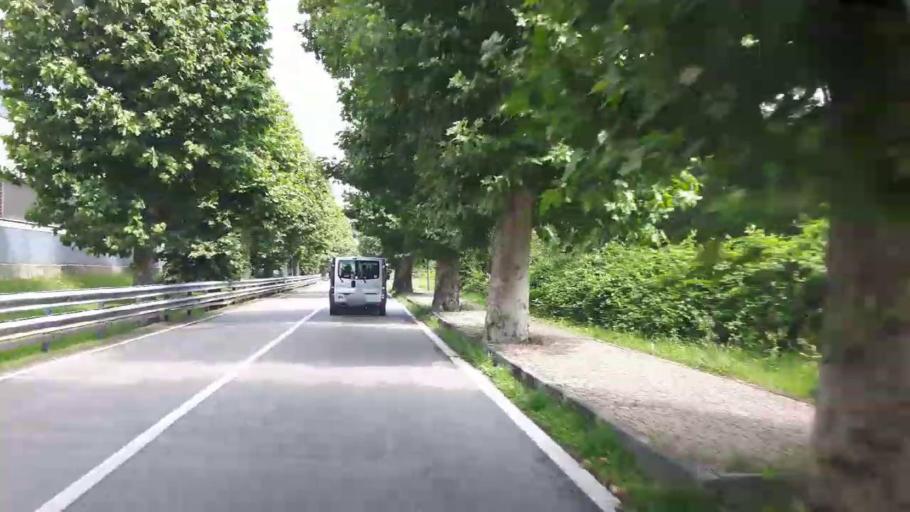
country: IT
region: Piedmont
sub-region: Provincia Verbano-Cusio-Ossola
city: Gravellona Toce
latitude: 45.9370
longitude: 8.4296
